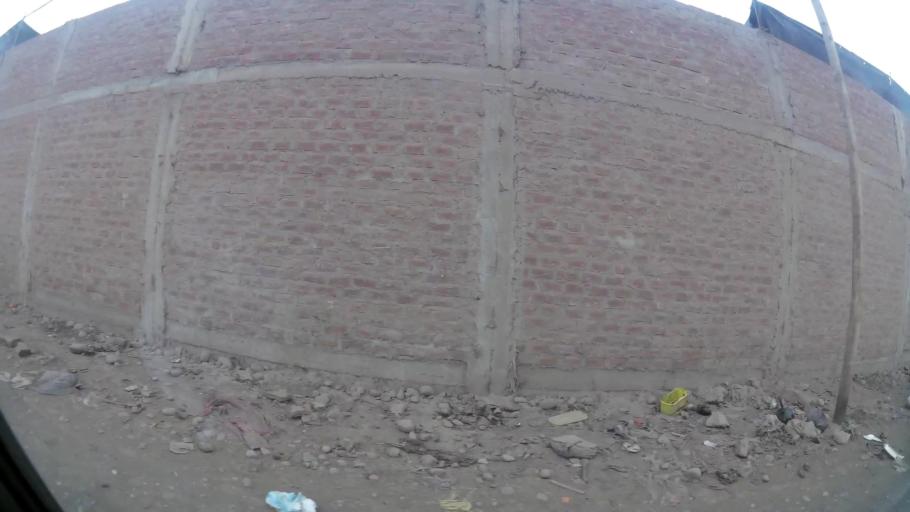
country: PE
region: Lima
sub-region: Provincia de Huaral
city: Huaral
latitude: -11.4972
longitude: -77.1982
